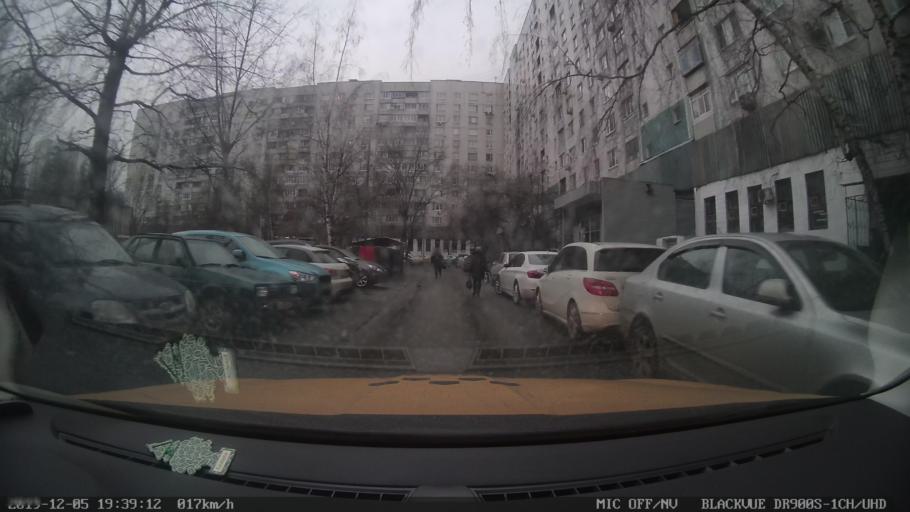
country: RU
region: Moscow
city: Lianozovo
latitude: 55.8941
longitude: 37.5909
